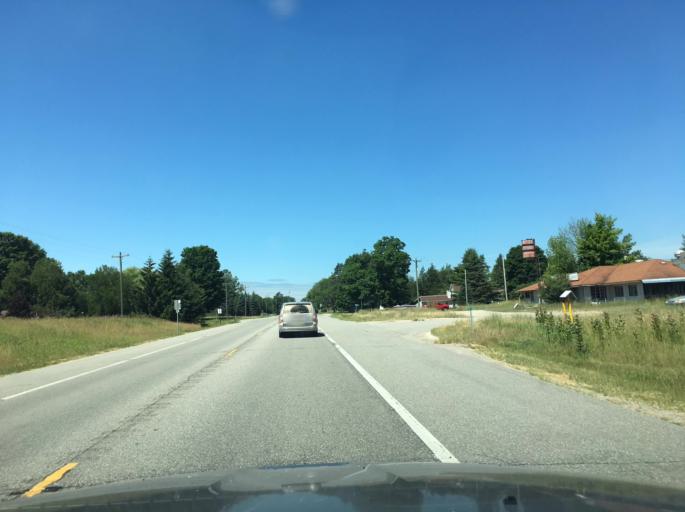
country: US
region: Michigan
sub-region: Osceola County
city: Reed City
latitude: 43.8875
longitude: -85.5413
